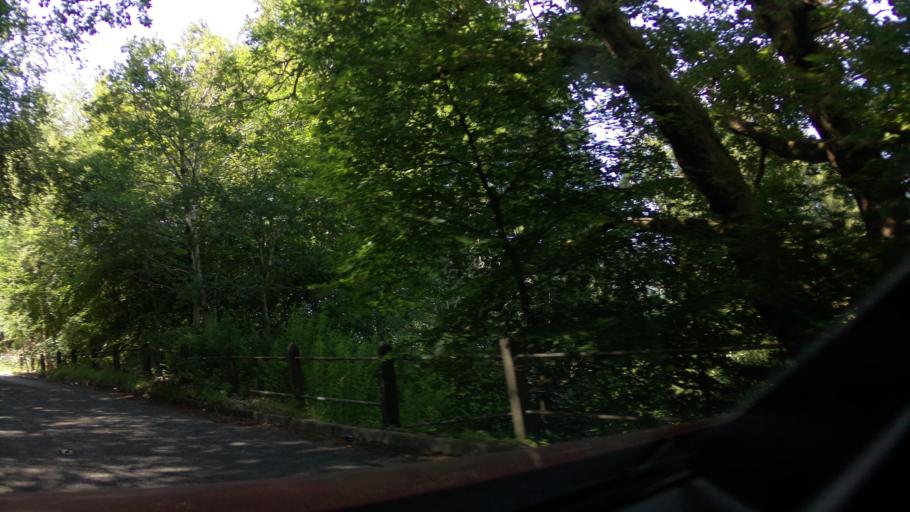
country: GB
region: Wales
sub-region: Caerphilly County Borough
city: New Tredegar
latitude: 51.7140
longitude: -3.2368
